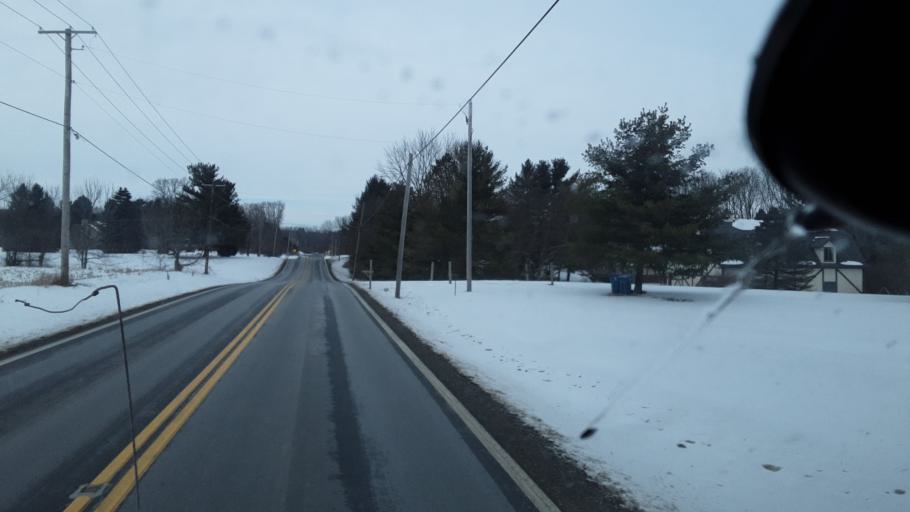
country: US
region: Ohio
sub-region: Delaware County
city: Delaware
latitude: 40.2348
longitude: -83.1523
